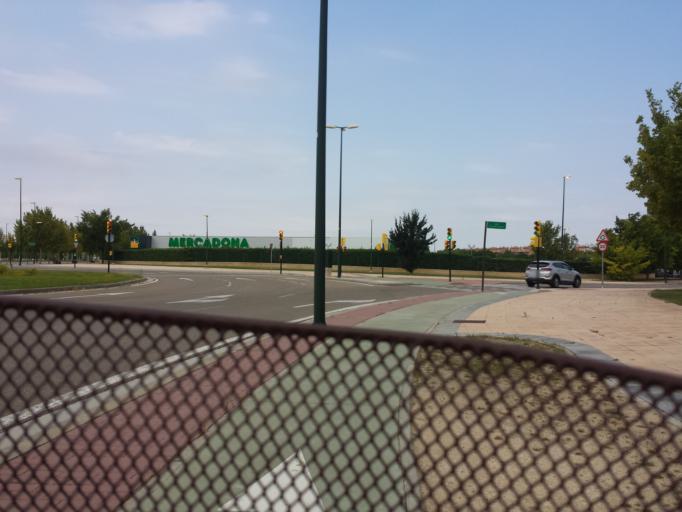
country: ES
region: Aragon
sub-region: Provincia de Zaragoza
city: Montecanal
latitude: 41.6219
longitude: -0.9356
